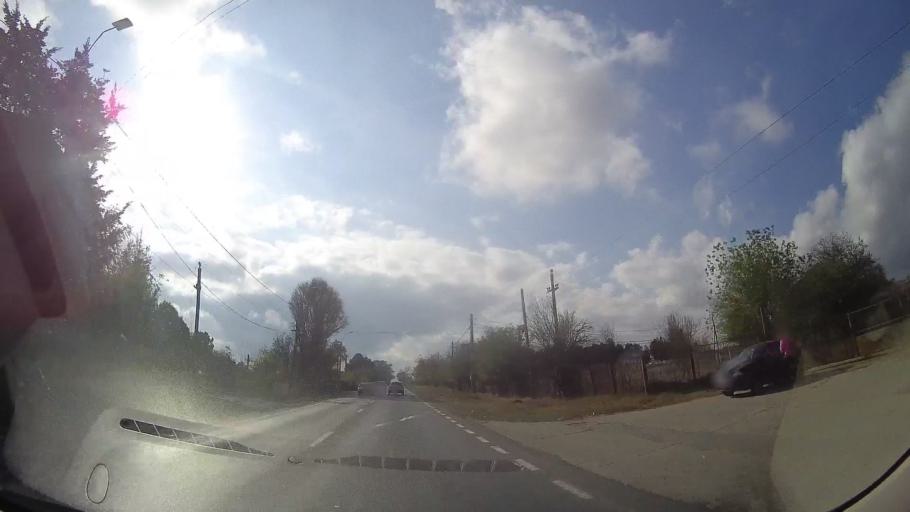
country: RO
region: Constanta
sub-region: Comuna Agigea
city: Agigea
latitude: 44.0873
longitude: 28.6091
